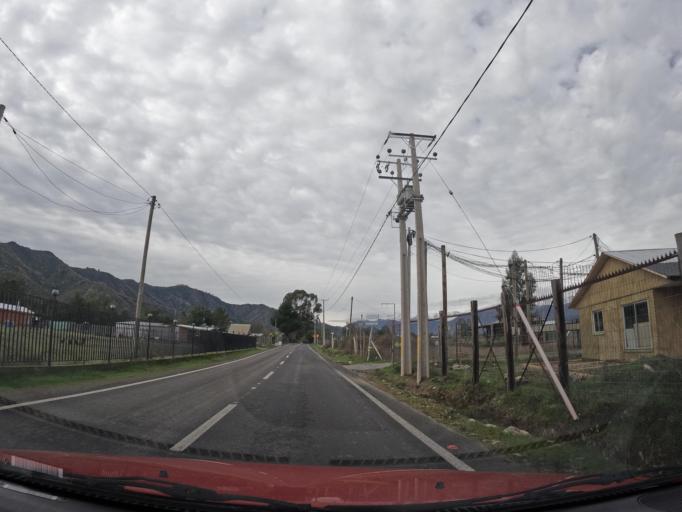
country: CL
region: Maule
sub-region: Provincia de Linares
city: Linares
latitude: -35.9249
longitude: -71.4174
